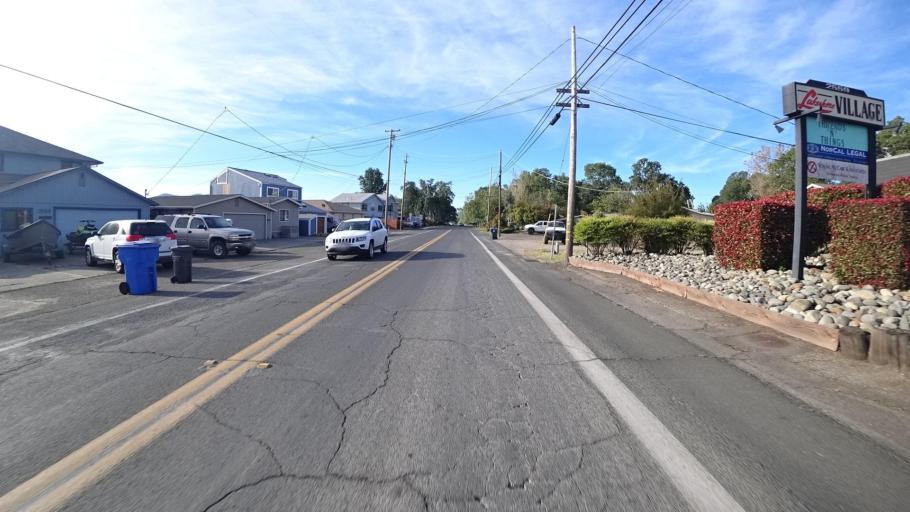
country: US
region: California
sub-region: Lake County
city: Lakeport
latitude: 39.0629
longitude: -122.9137
